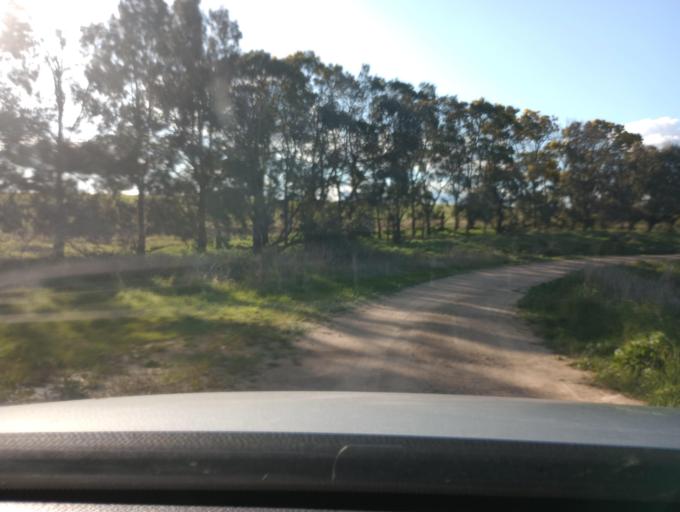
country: AU
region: New South Wales
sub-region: Blayney
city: Millthorpe
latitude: -33.4068
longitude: 149.3077
